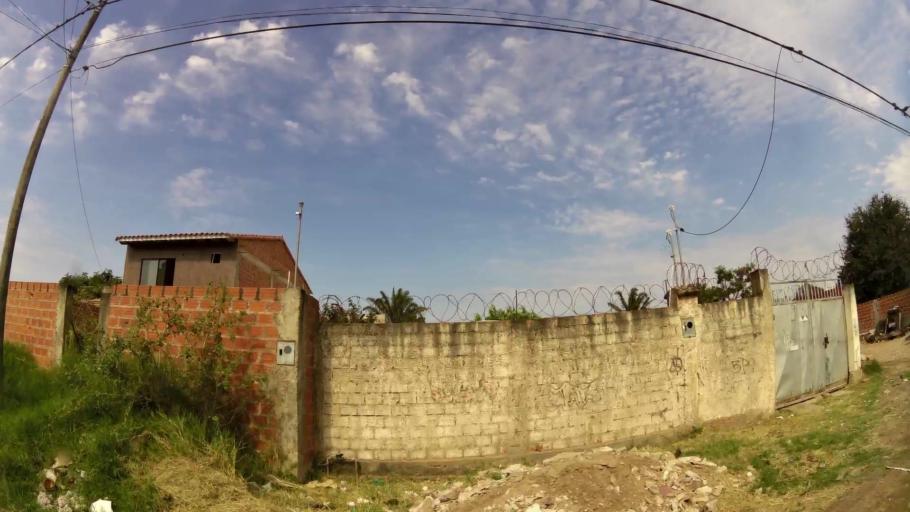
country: BO
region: Santa Cruz
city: Santa Cruz de la Sierra
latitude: -17.7231
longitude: -63.1367
